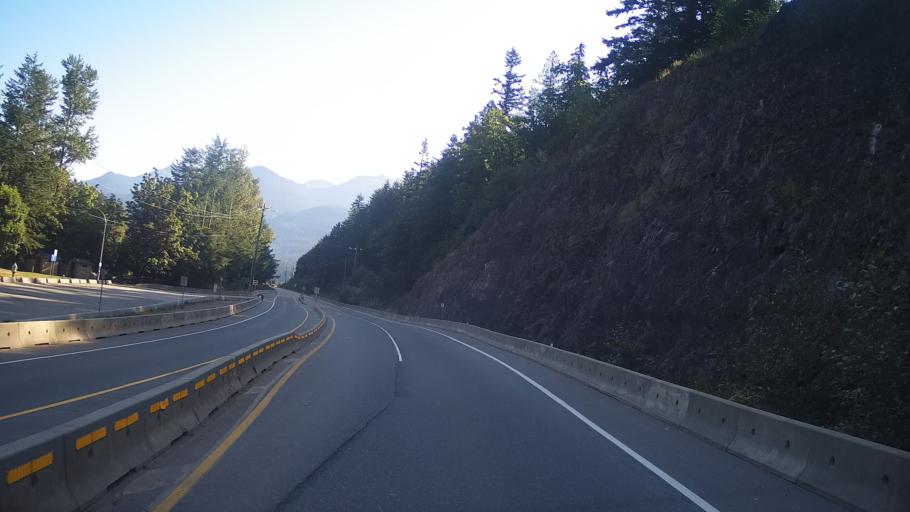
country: CA
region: British Columbia
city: Hope
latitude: 49.4092
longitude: -121.4460
